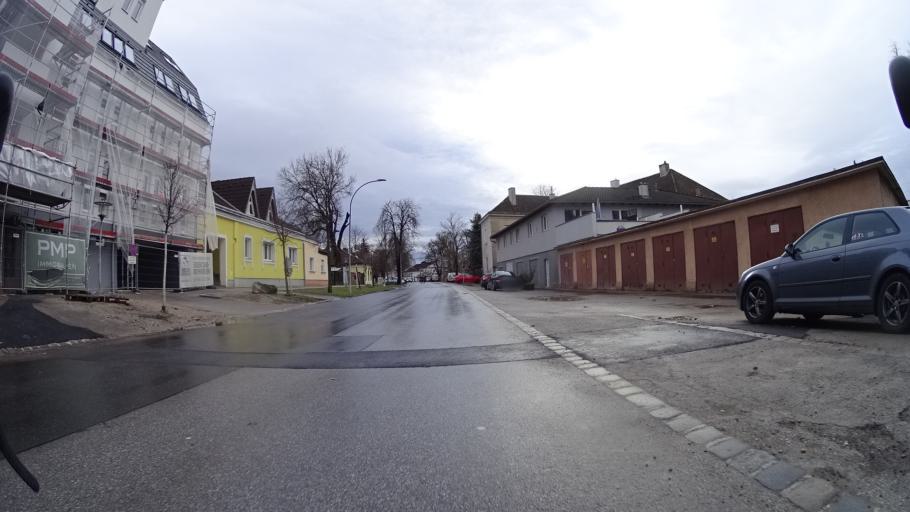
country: AT
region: Lower Austria
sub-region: Politischer Bezirk Korneuburg
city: Korneuburg
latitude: 48.3434
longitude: 16.3302
